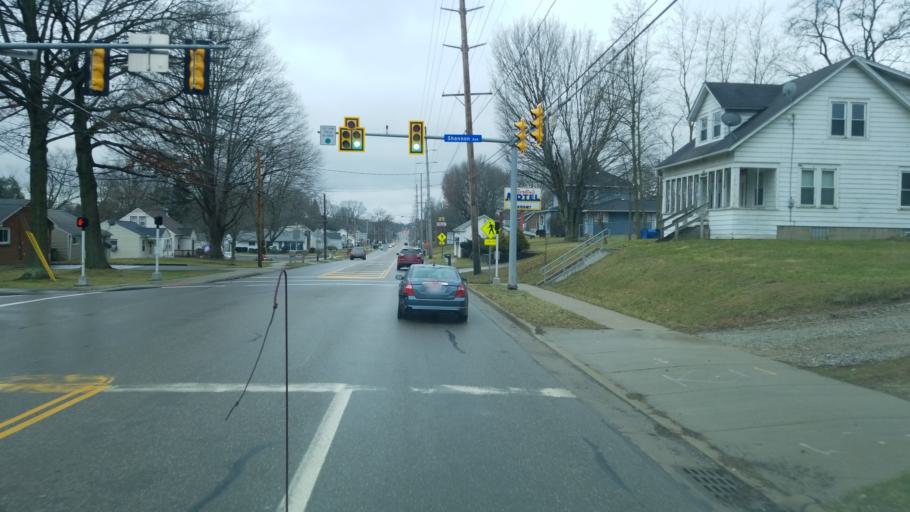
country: US
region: Ohio
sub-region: Summit County
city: Norton
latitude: 41.0158
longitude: -81.6385
